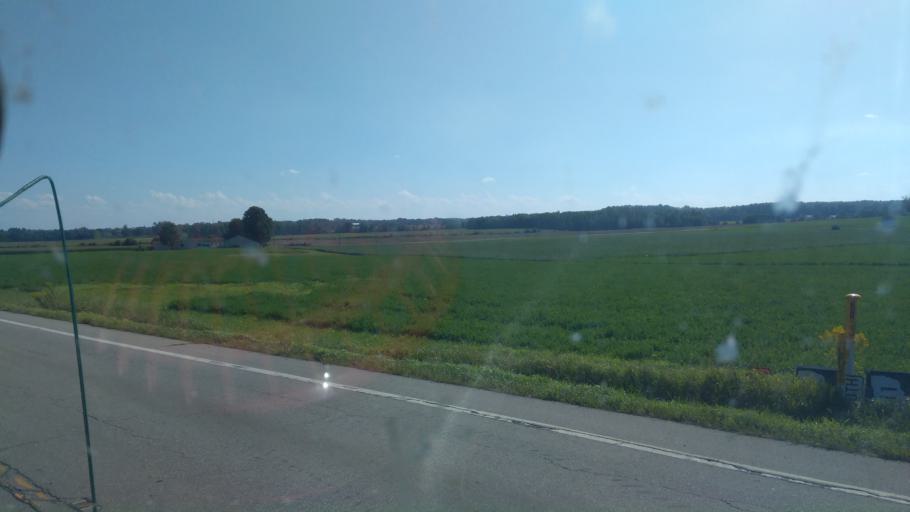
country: US
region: Ohio
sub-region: Ashland County
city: Ashland
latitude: 40.9270
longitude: -82.3487
